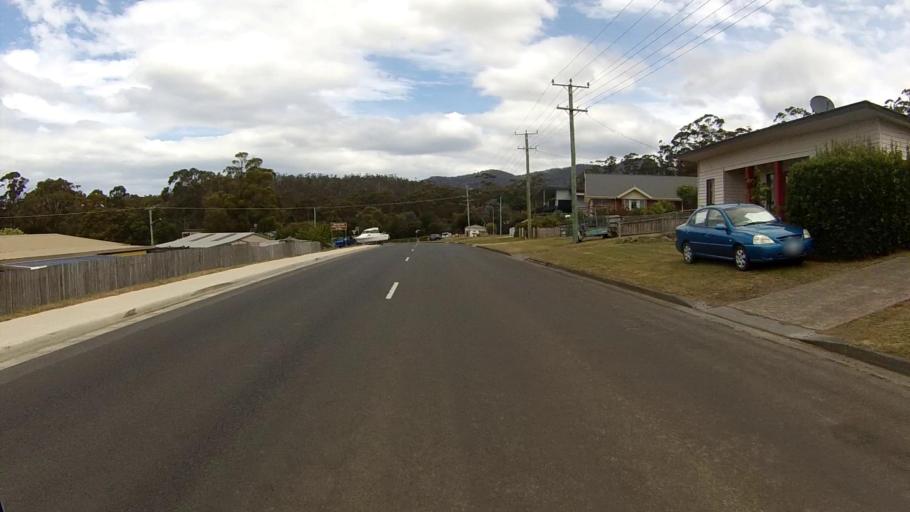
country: AU
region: Tasmania
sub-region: Sorell
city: Sorell
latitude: -42.5655
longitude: 147.8735
